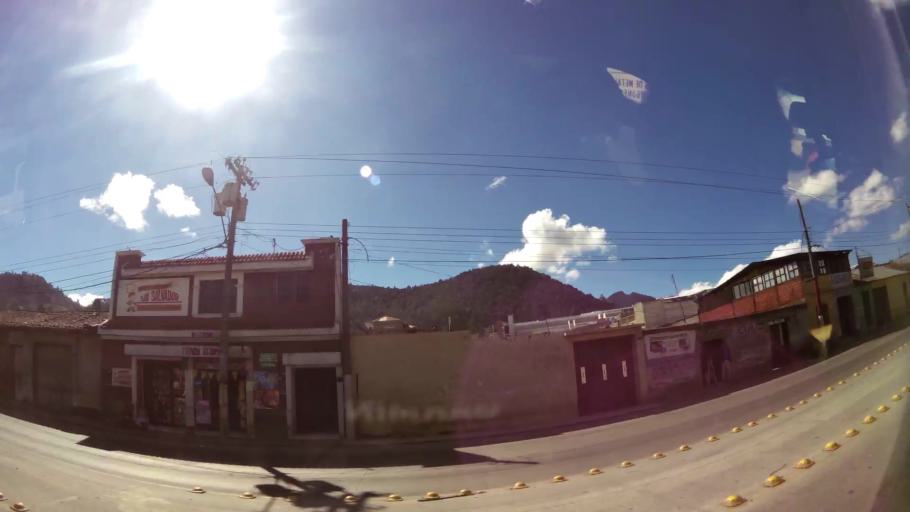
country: GT
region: Quetzaltenango
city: Quetzaltenango
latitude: 14.8403
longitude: -91.5020
